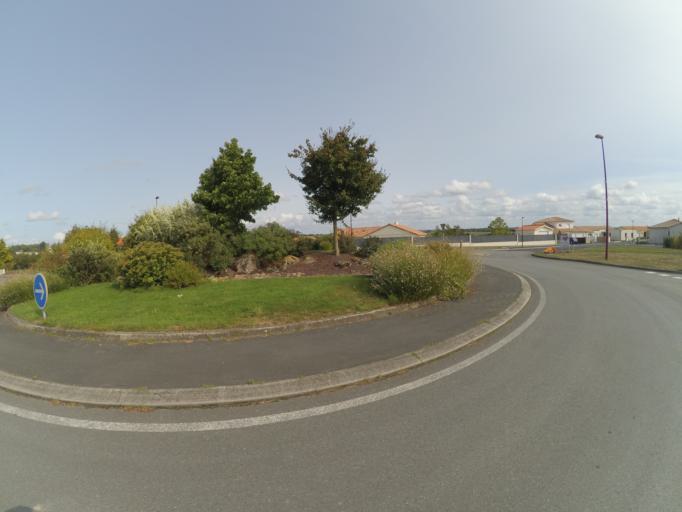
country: FR
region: Pays de la Loire
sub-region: Departement de Maine-et-Loire
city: Torfou
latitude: 47.0323
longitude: -1.1242
